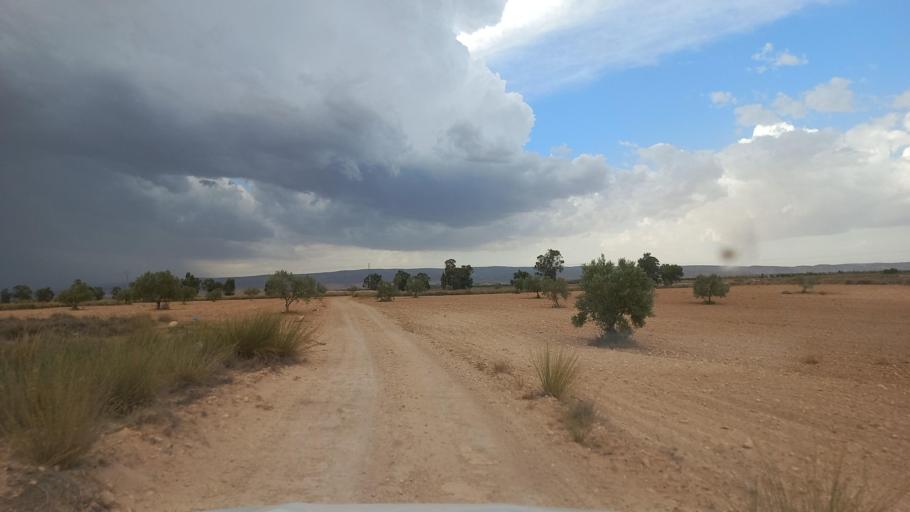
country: TN
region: Al Qasrayn
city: Kasserine
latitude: 35.2472
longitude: 9.0035
